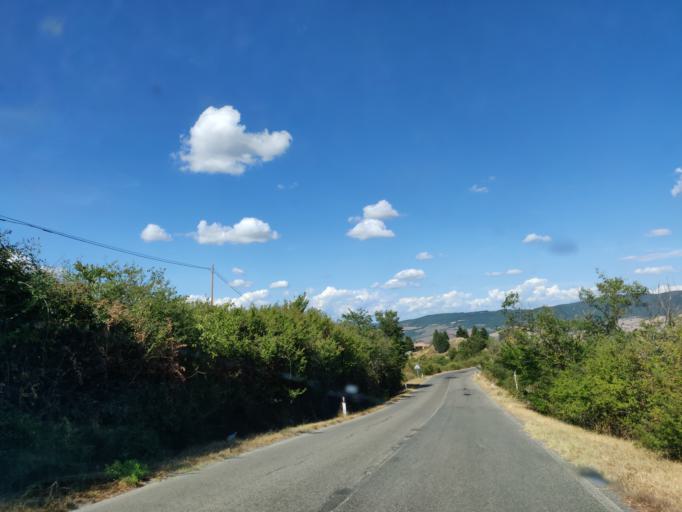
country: IT
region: Tuscany
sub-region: Provincia di Siena
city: Radicofani
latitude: 42.9684
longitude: 11.7341
